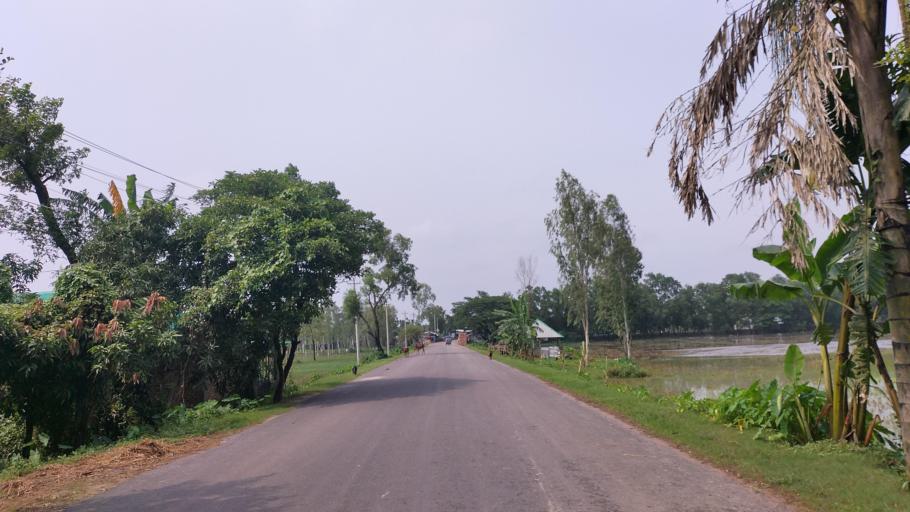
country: BD
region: Dhaka
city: Netrakona
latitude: 24.9498
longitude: 90.8324
